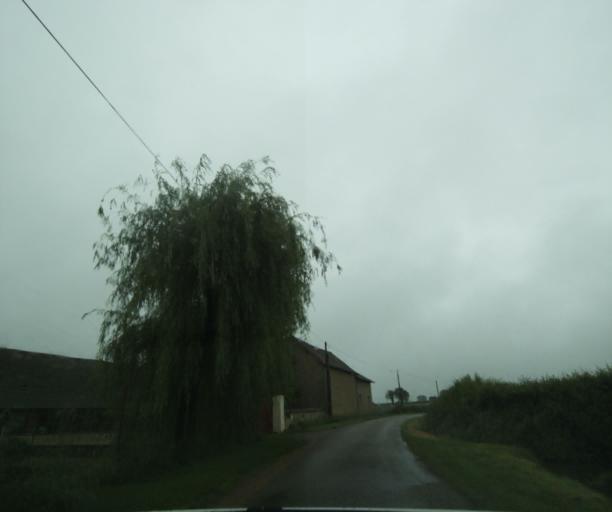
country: FR
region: Bourgogne
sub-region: Departement de Saone-et-Loire
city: Paray-le-Monial
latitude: 46.4102
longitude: 4.1737
